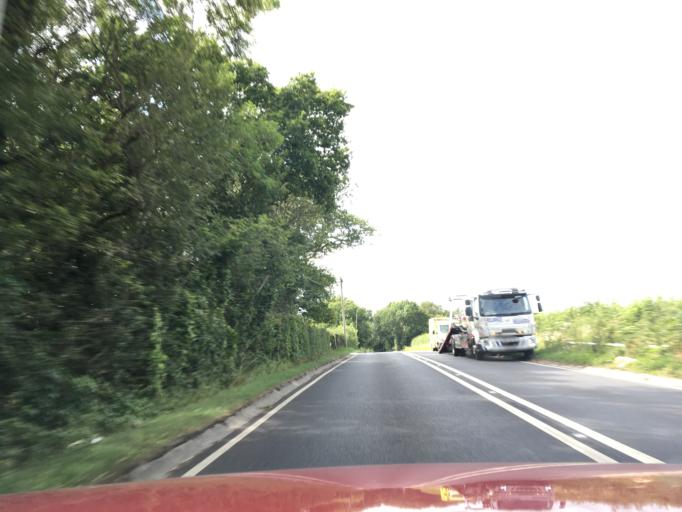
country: GB
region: England
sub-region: Kent
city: Edenbridge
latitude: 51.1317
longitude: 0.1001
